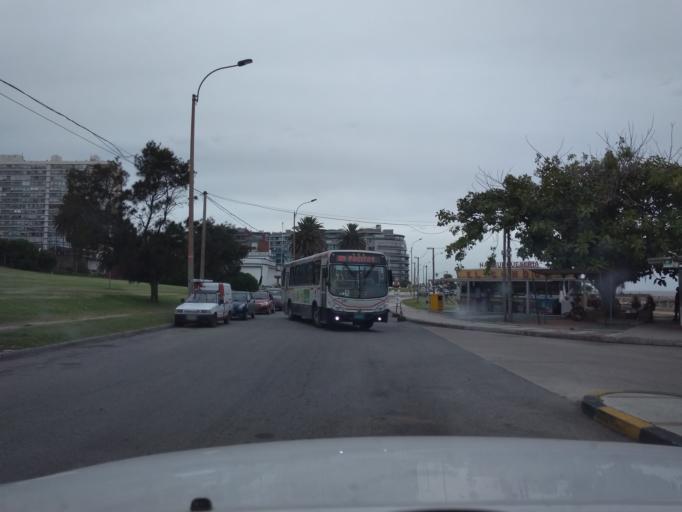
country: UY
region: Montevideo
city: Montevideo
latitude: -34.9111
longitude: -56.1372
